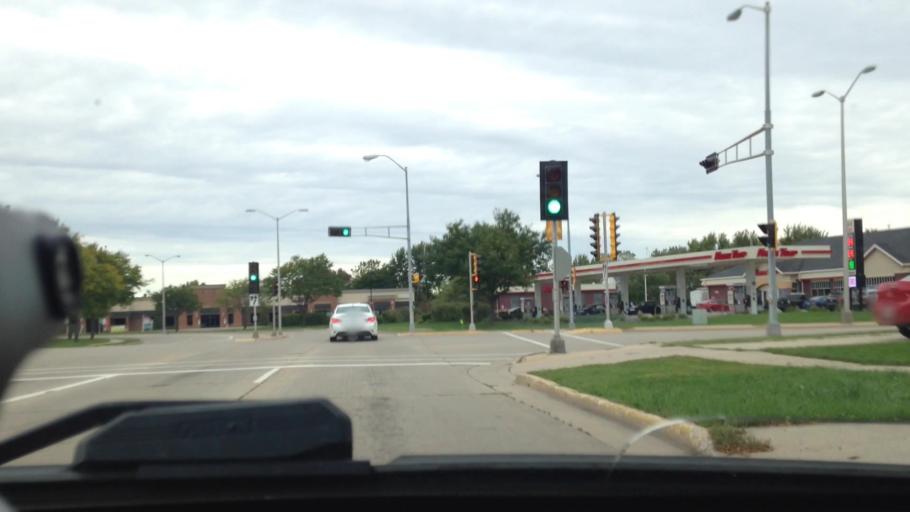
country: US
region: Wisconsin
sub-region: Fond du Lac County
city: North Fond du Lac
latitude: 43.7913
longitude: -88.4730
